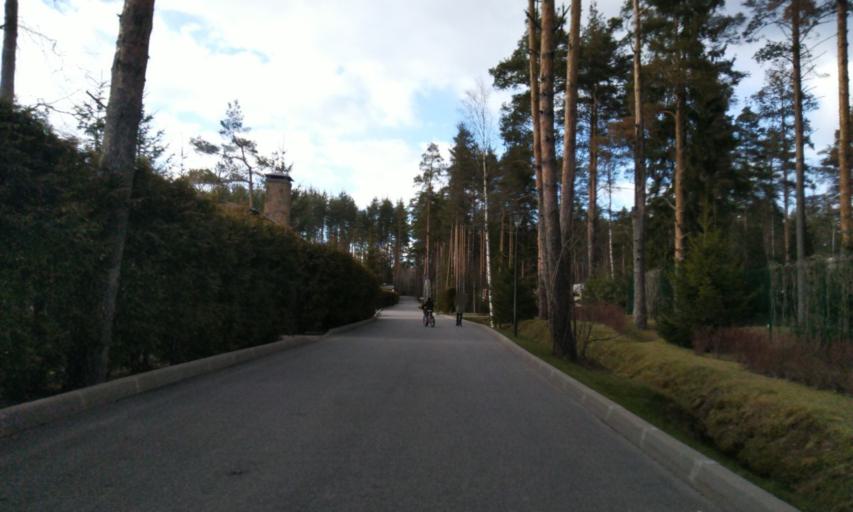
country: RU
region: Leningrad
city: Novoye Devyatkino
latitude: 60.1285
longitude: 30.4457
